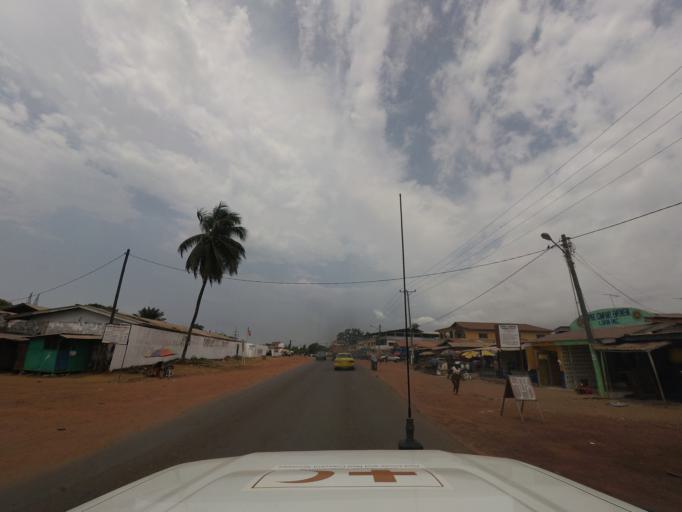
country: LR
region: Montserrado
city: Monrovia
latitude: 6.2673
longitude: -10.6949
